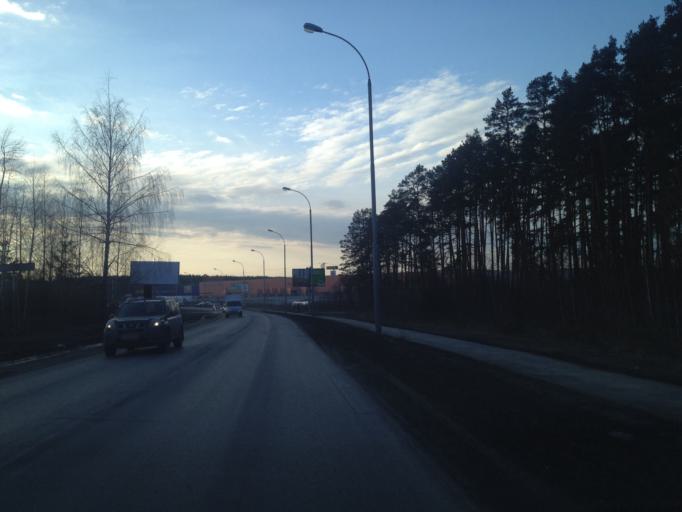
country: RU
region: Sverdlovsk
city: Shirokaya Rechka
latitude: 56.8193
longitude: 60.5098
